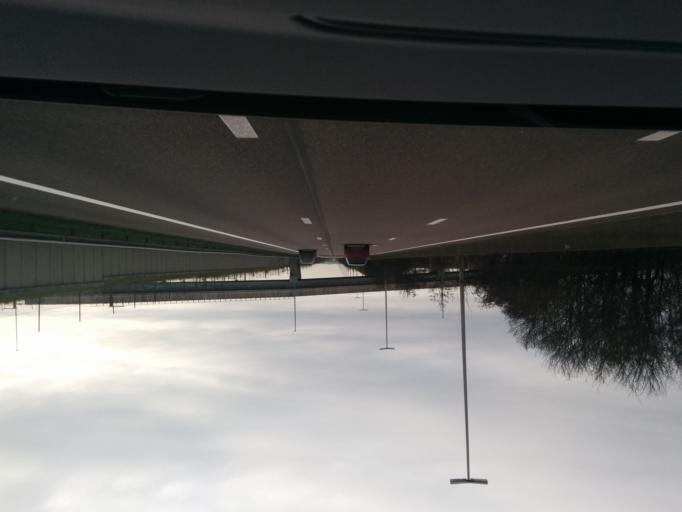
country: BE
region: Flanders
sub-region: Provincie Vlaams-Brabant
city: Boutersem
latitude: 50.8141
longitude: 4.8562
